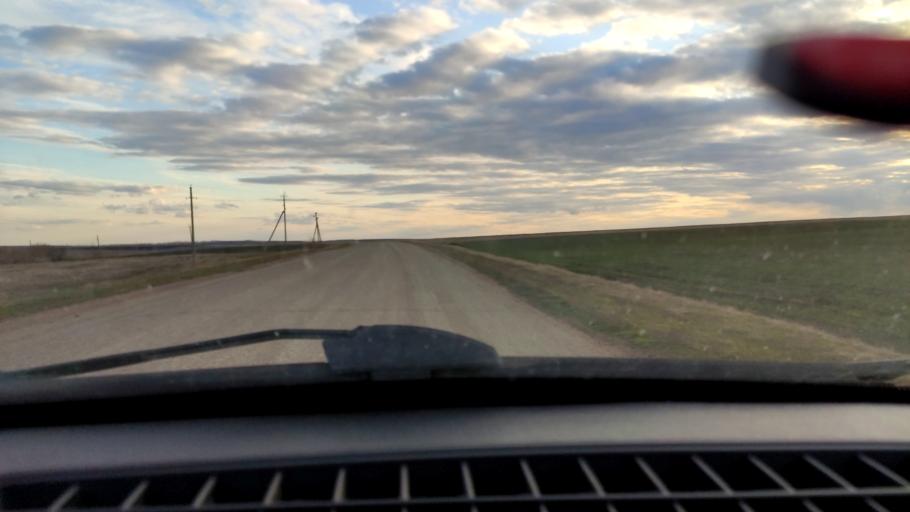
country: RU
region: Bashkortostan
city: Tolbazy
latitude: 54.0022
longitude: 55.6801
